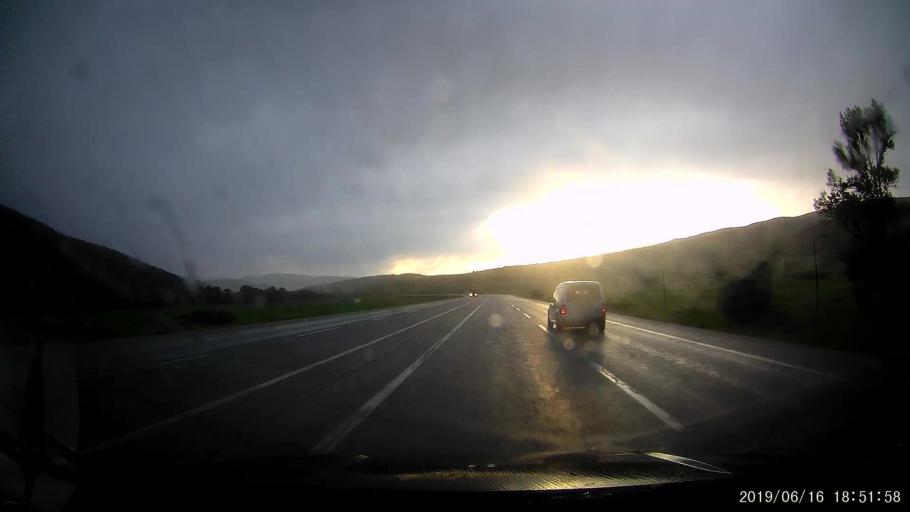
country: TR
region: Erzincan
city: Catalcam
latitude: 39.9021
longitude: 38.9145
